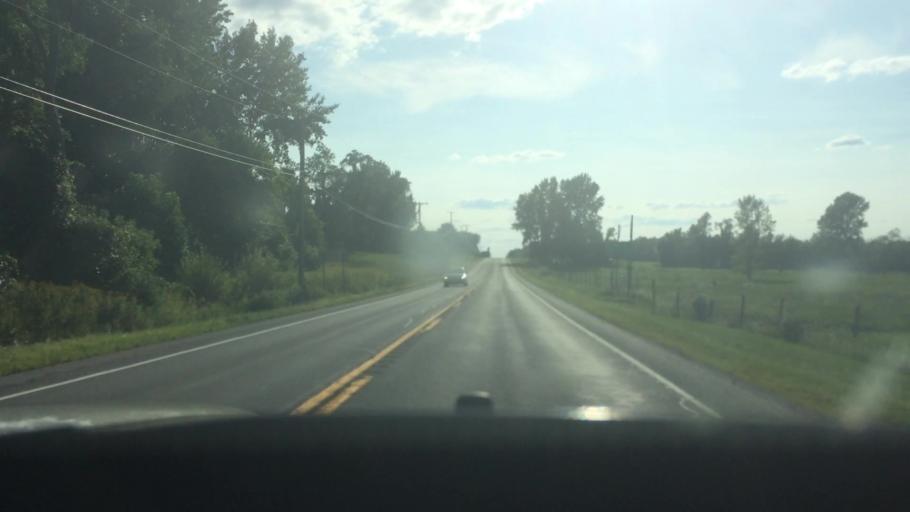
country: US
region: New York
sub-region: St. Lawrence County
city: Potsdam
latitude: 44.6823
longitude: -74.8164
